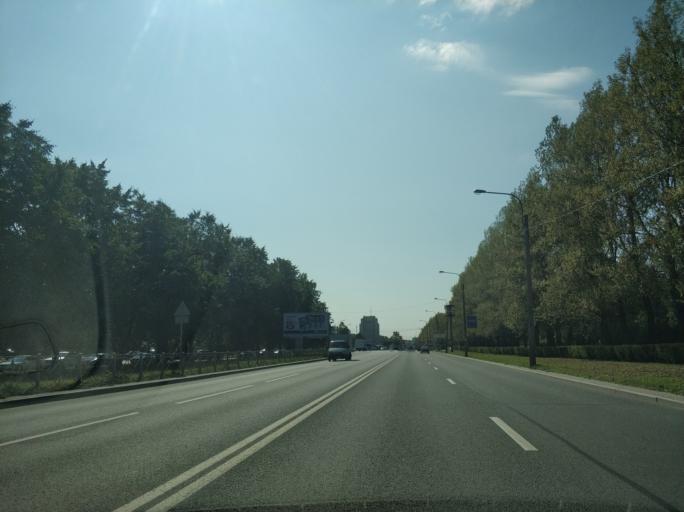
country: RU
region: St.-Petersburg
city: Kupchino
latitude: 59.8544
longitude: 30.3374
